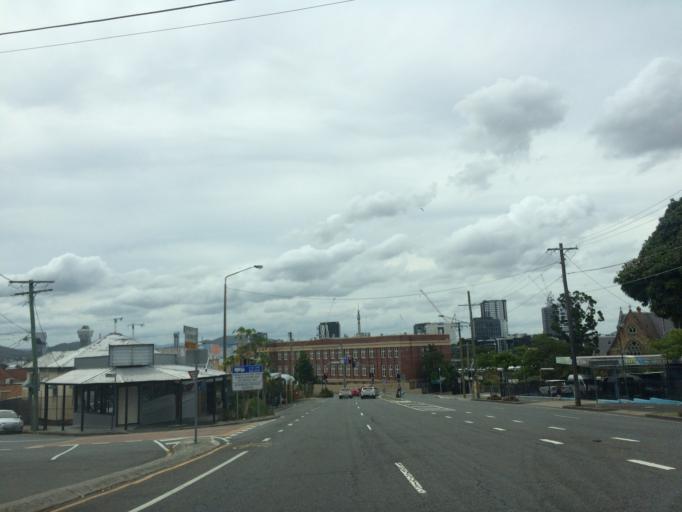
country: AU
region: Queensland
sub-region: Brisbane
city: South Brisbane
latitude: -27.4830
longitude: 153.0195
